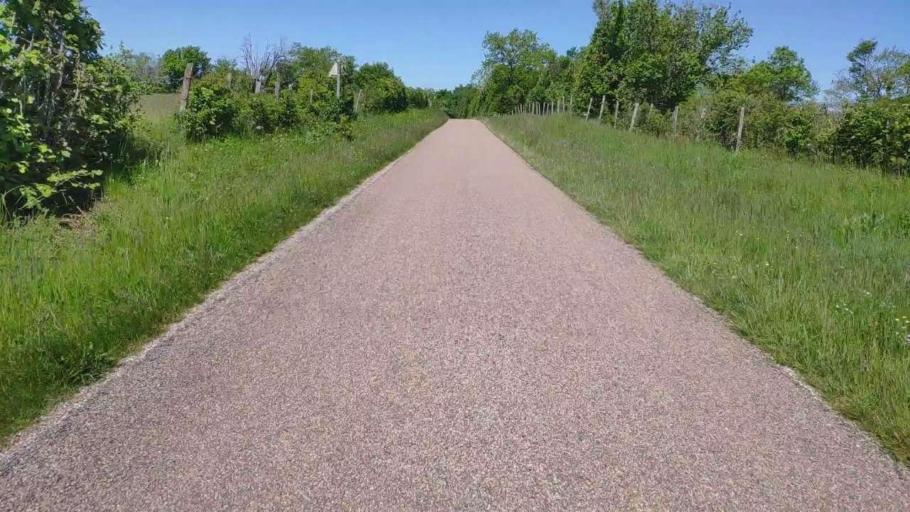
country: FR
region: Franche-Comte
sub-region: Departement du Jura
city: Poligny
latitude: 46.7333
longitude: 5.7260
